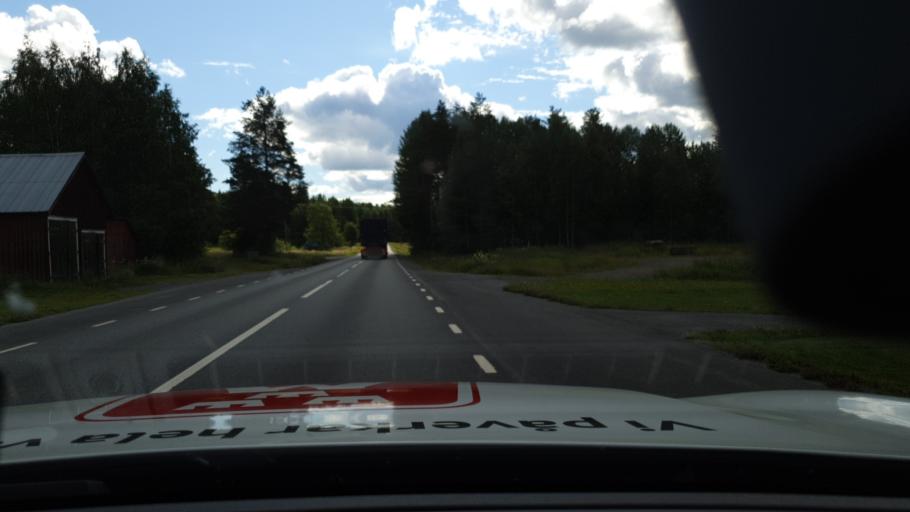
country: SE
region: Norrbotten
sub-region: Lulea Kommun
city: Sodra Sunderbyn
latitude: 65.8299
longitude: 21.9673
